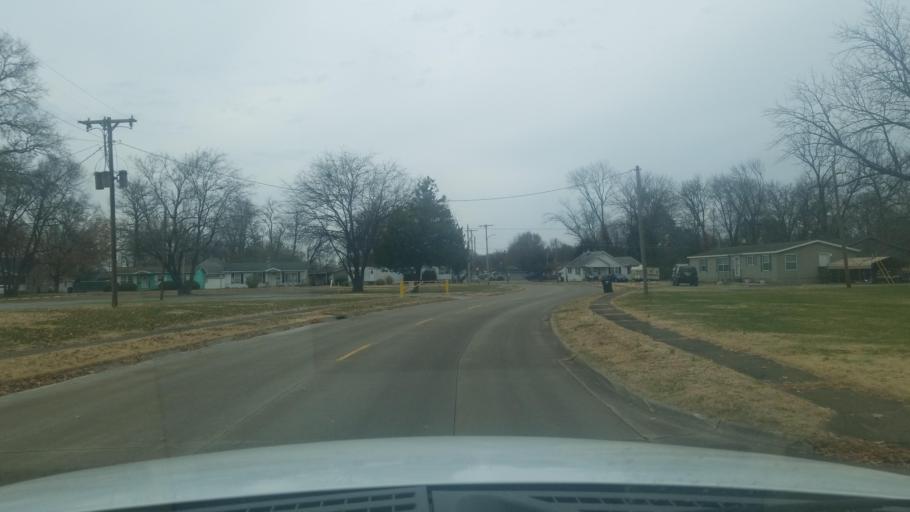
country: US
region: Illinois
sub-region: Saline County
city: Harrisburg
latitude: 37.7352
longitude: -88.5528
